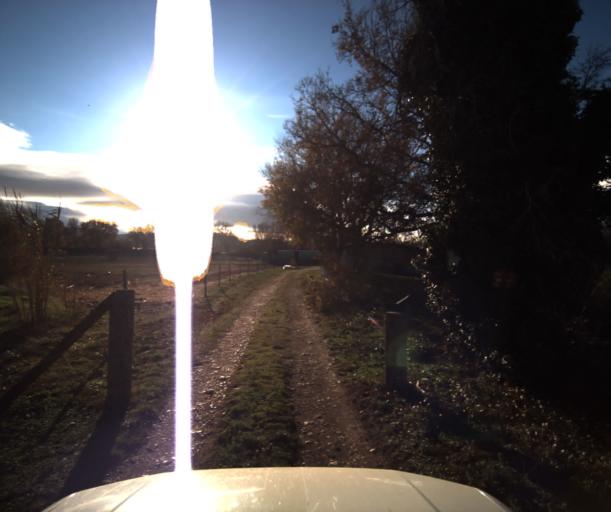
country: FR
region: Provence-Alpes-Cote d'Azur
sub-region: Departement des Bouches-du-Rhone
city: Le Puy-Sainte-Reparade
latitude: 43.6814
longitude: 5.4668
